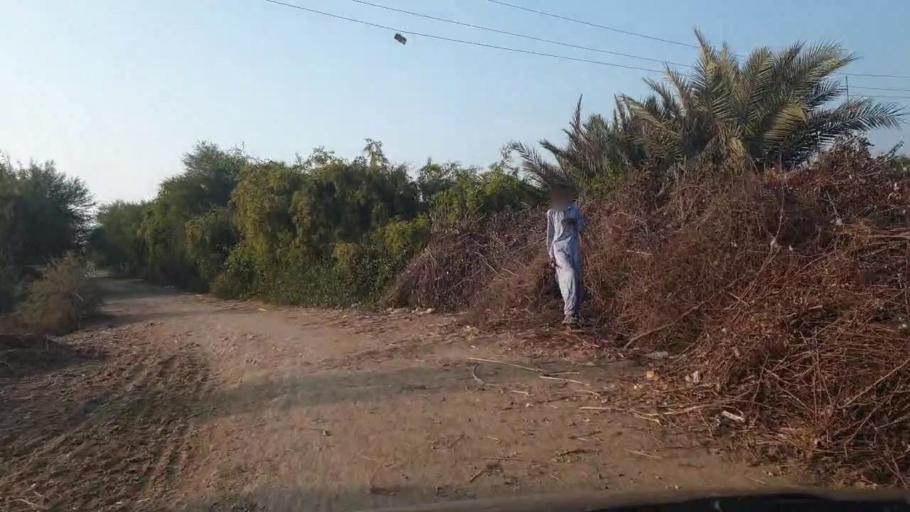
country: PK
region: Sindh
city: Berani
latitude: 25.8616
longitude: 68.7335
